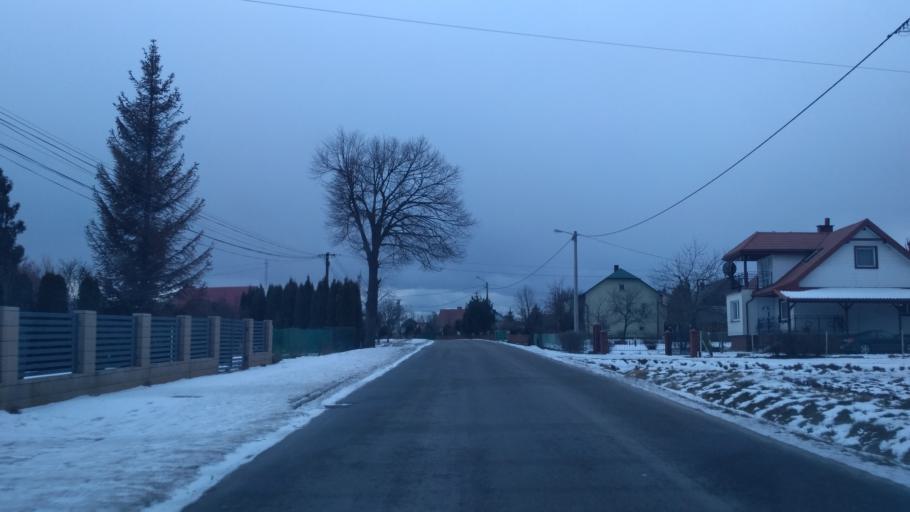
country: PL
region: Subcarpathian Voivodeship
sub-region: Powiat brzozowski
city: Wesola
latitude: 49.8347
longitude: 22.0891
